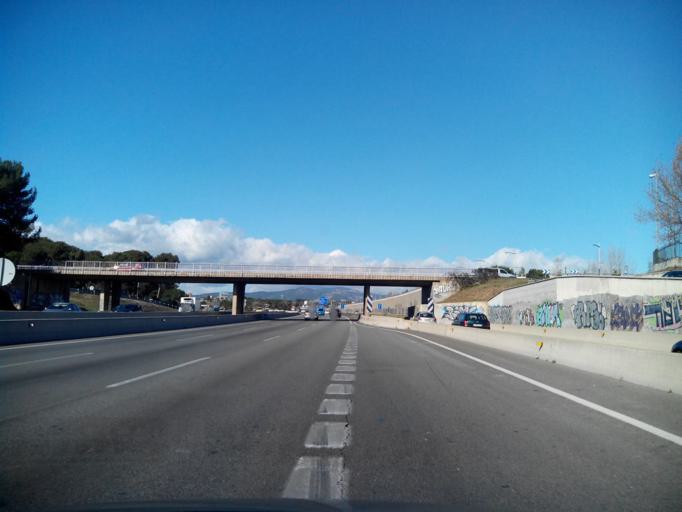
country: ES
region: Catalonia
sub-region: Provincia de Barcelona
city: Sant Quirze del Valles
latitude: 41.5358
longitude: 2.0870
